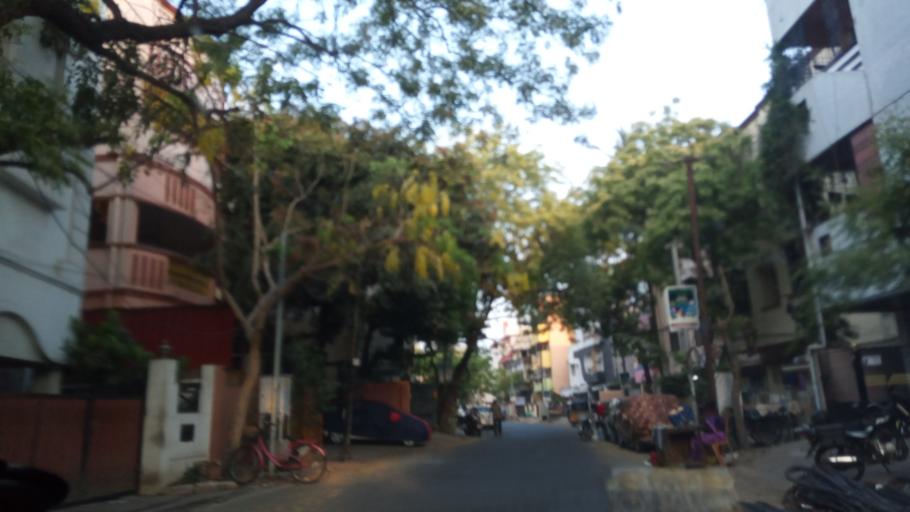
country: IN
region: Tamil Nadu
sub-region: Chennai
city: Chetput
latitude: 13.0392
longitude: 80.2196
